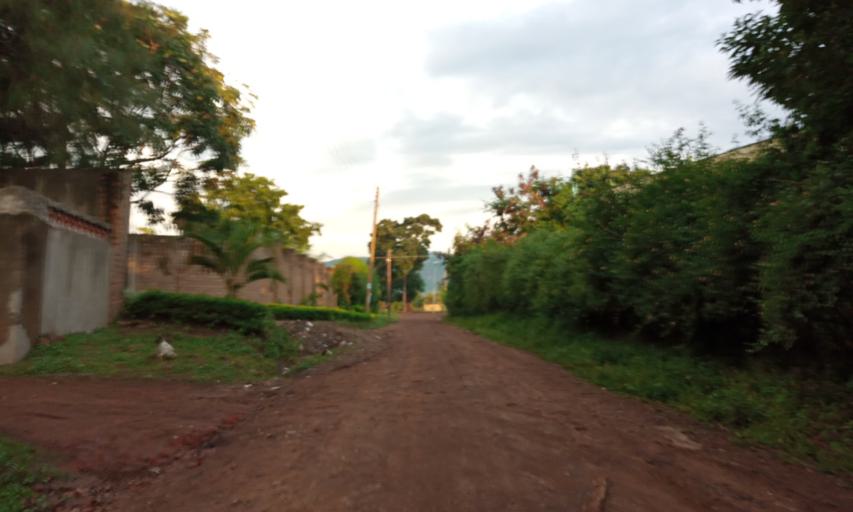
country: UG
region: Eastern Region
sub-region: Mbale District
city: Mbale
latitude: 1.0678
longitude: 34.1805
